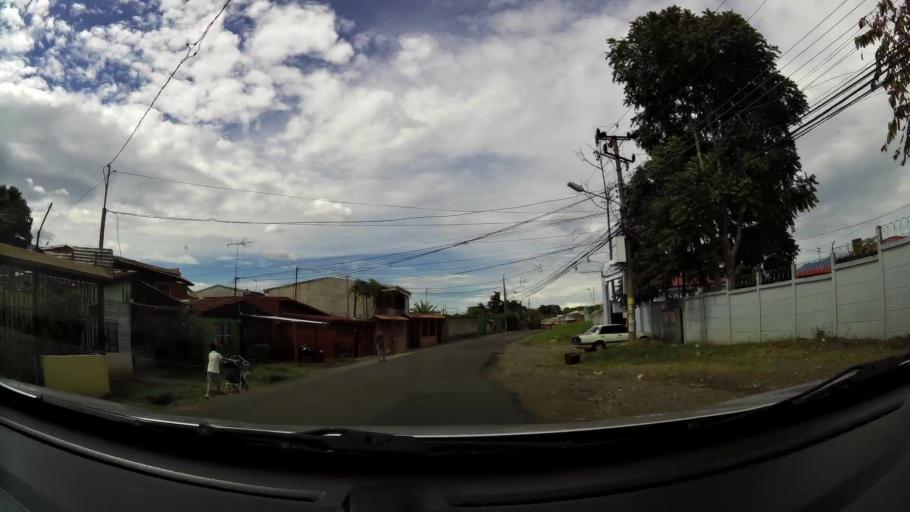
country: CR
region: San Jose
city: San Rafael Arriba
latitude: 9.8968
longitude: -84.0760
